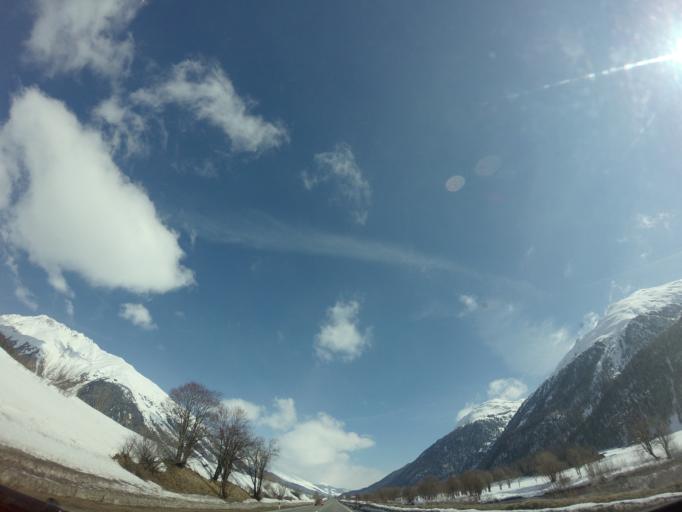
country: CH
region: Grisons
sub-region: Maloja District
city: Samedan
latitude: 46.5377
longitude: 9.8829
